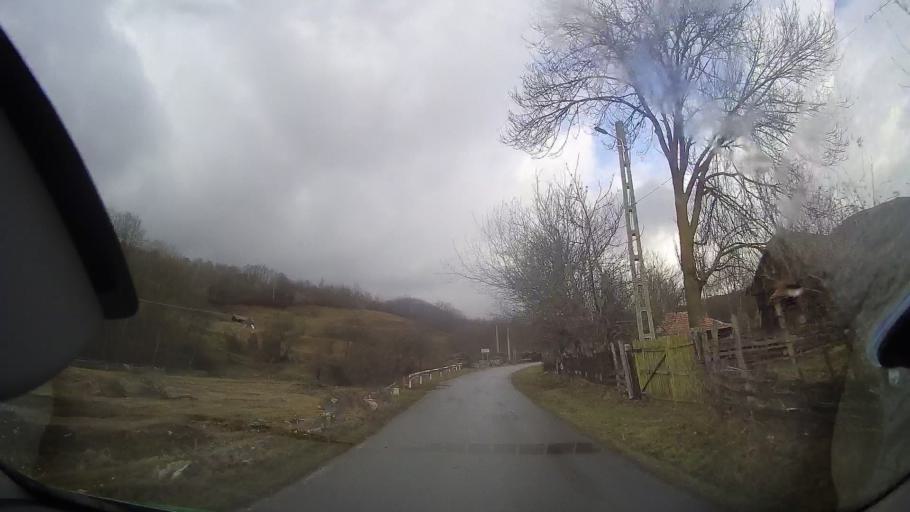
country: RO
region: Alba
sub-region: Comuna Ocolis
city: Ocolis
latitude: 46.4919
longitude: 23.4572
